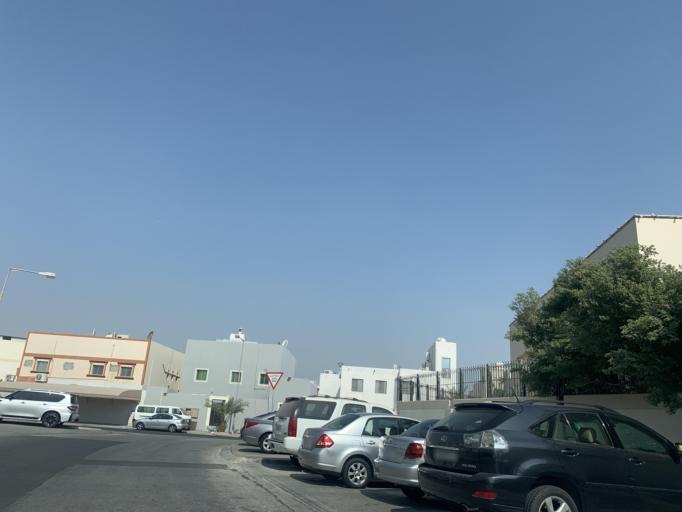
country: BH
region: Central Governorate
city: Madinat Hamad
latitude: 26.1250
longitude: 50.4936
